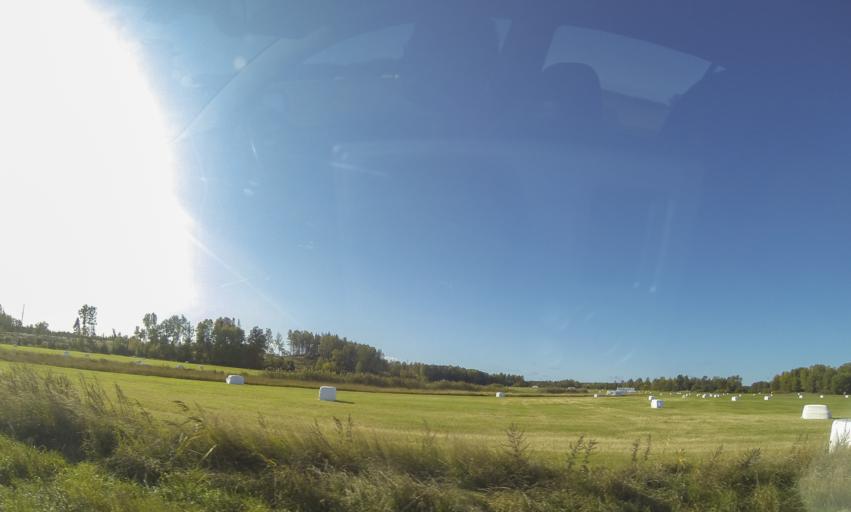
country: SE
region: Soedermanland
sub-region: Eskilstuna Kommun
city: Kvicksund
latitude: 59.5022
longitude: 16.3544
